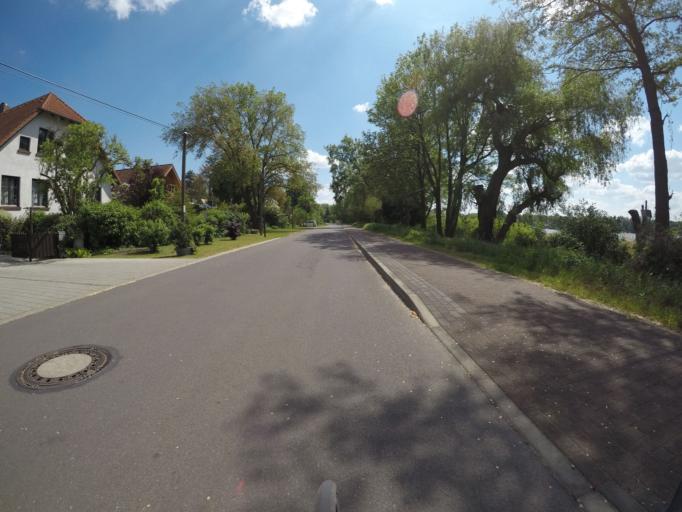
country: DE
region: Brandenburg
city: Werder
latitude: 52.3618
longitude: 12.9620
